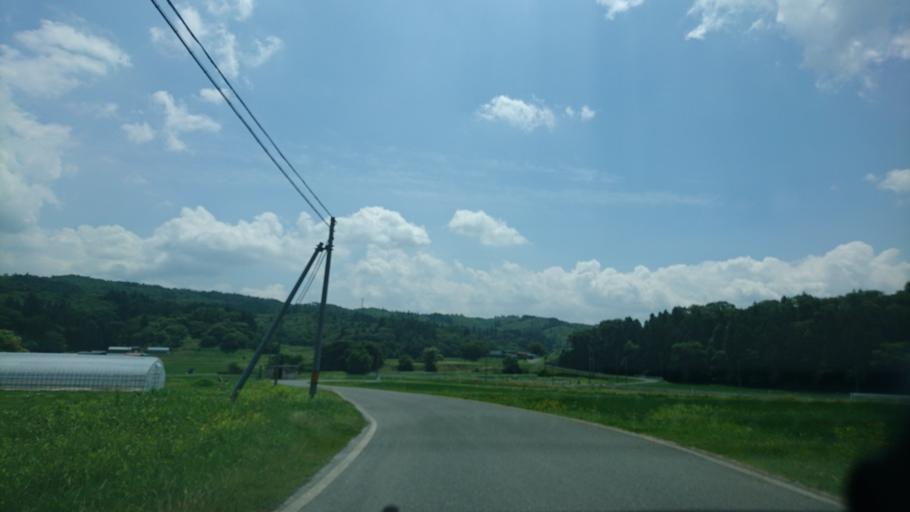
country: JP
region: Iwate
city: Ichinoseki
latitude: 38.9116
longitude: 141.2227
